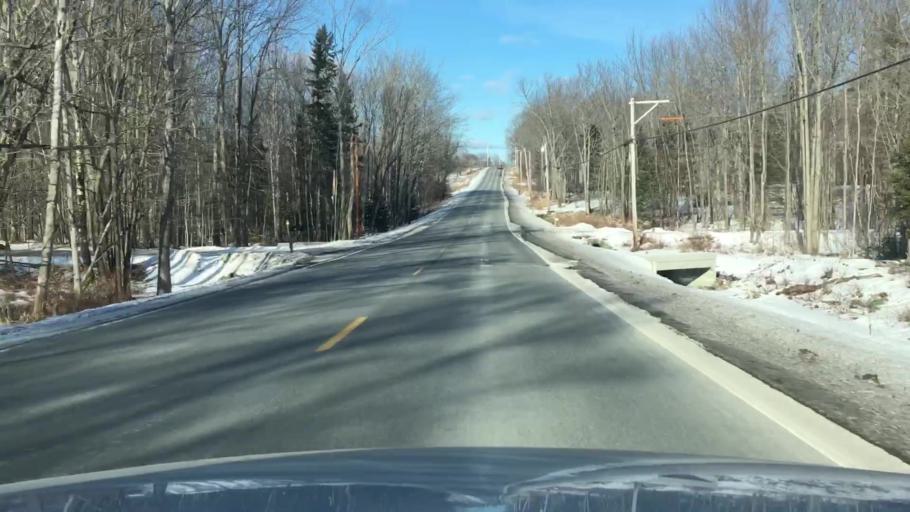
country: US
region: Maine
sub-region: Penobscot County
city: Holden
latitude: 44.7610
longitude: -68.5954
